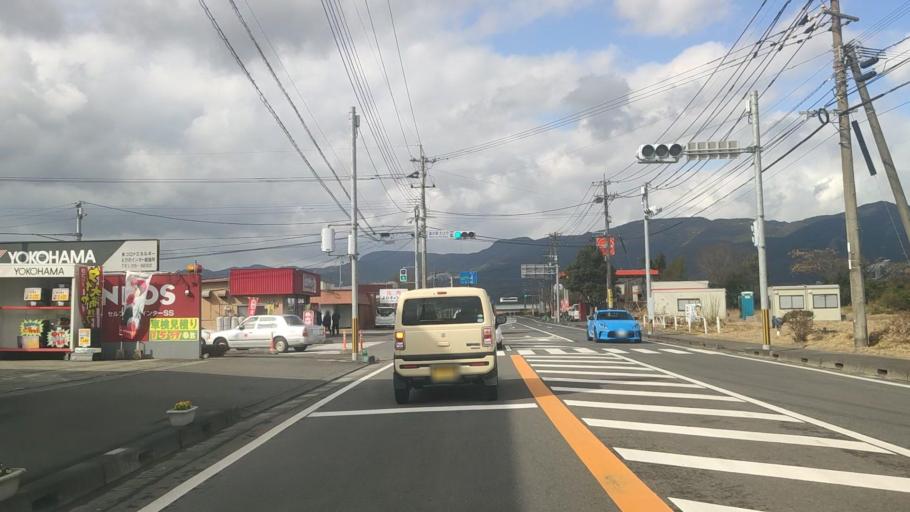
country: JP
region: Kumamoto
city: Hitoyoshi
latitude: 32.0509
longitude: 130.8063
